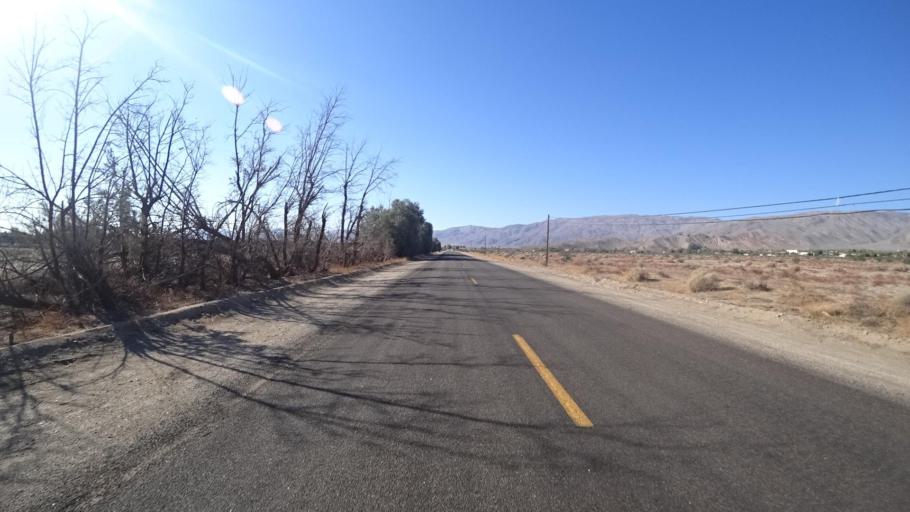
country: US
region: California
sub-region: San Diego County
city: Borrego Springs
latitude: 33.2692
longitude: -116.3750
